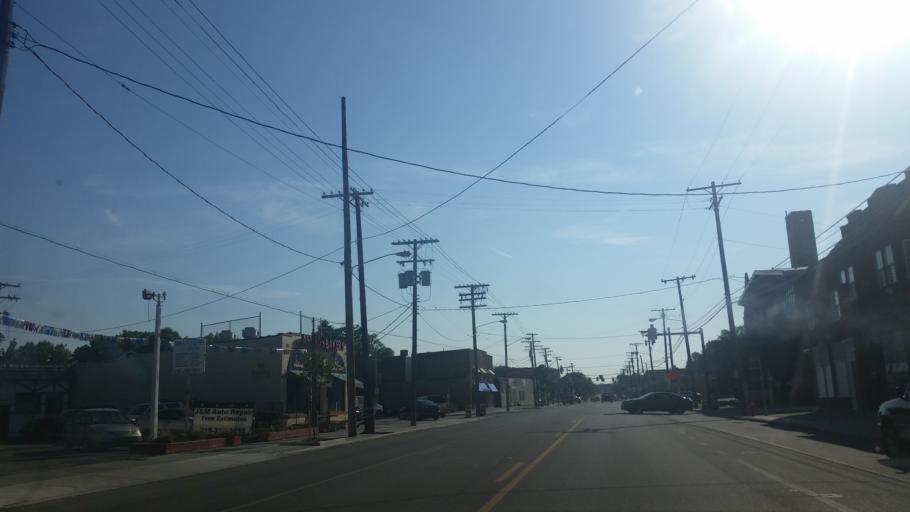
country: US
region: Ohio
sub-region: Cuyahoga County
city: Lakewood
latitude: 41.4594
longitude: -81.7769
